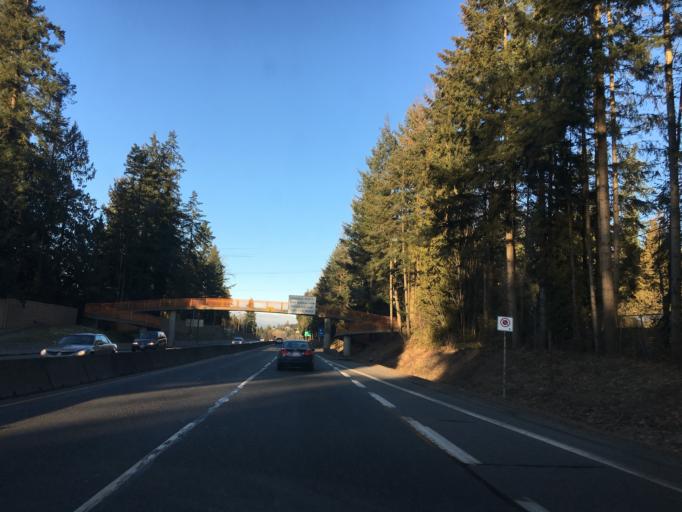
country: CA
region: British Columbia
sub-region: Fraser Valley Regional District
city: North Vancouver
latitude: 49.3326
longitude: -123.1064
